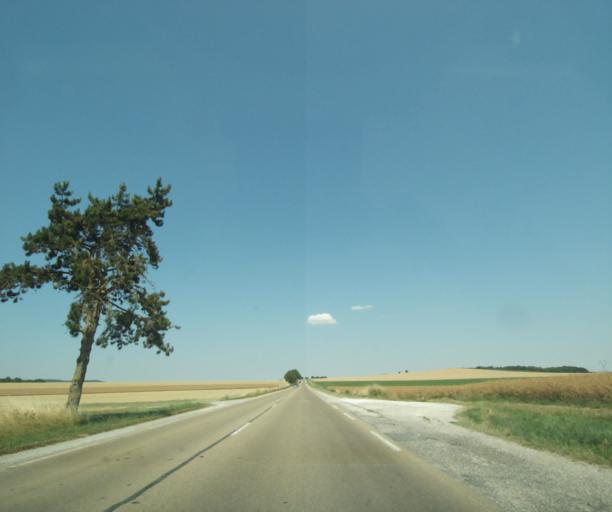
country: FR
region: Champagne-Ardenne
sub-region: Departement de la Marne
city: Verzy
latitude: 49.1265
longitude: 4.2400
